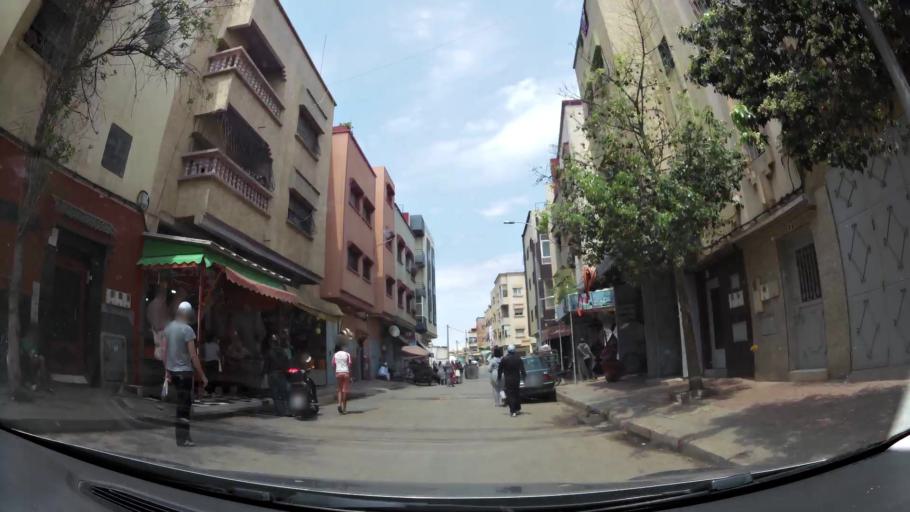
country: MA
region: Rabat-Sale-Zemmour-Zaer
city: Sale
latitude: 34.0546
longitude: -6.8146
